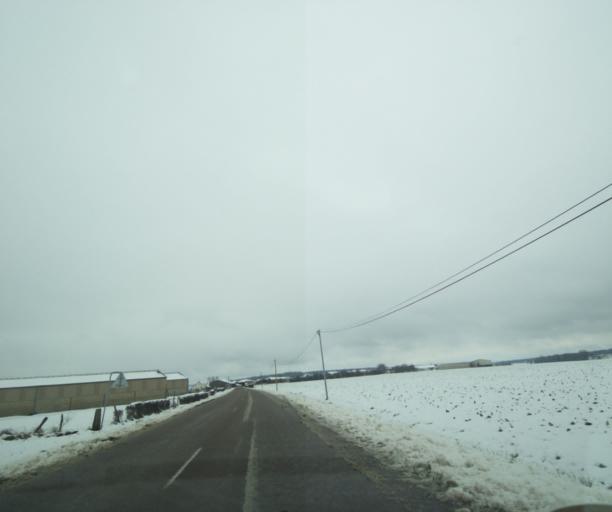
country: FR
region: Champagne-Ardenne
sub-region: Departement de la Haute-Marne
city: Montier-en-Der
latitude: 48.4452
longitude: 4.8013
